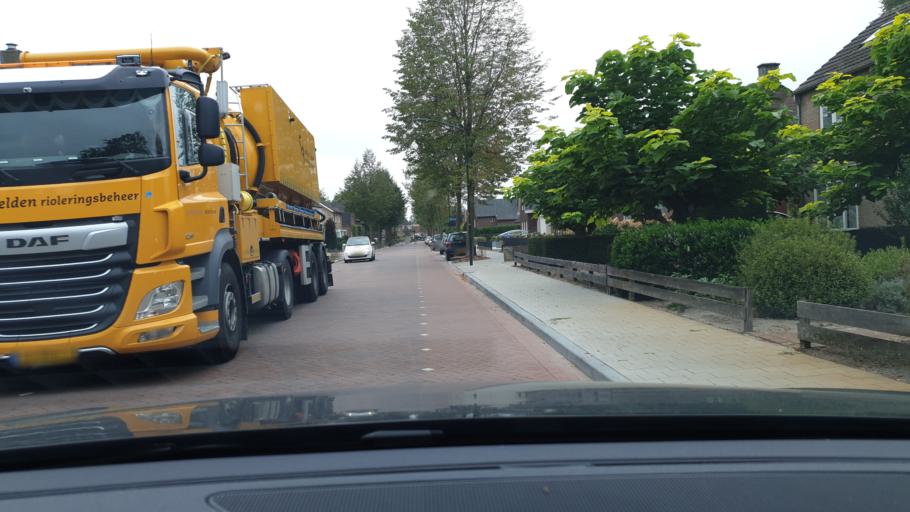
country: NL
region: North Brabant
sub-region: Gemeente Bladel en Netersel
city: Bladel
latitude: 51.3701
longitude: 5.2595
